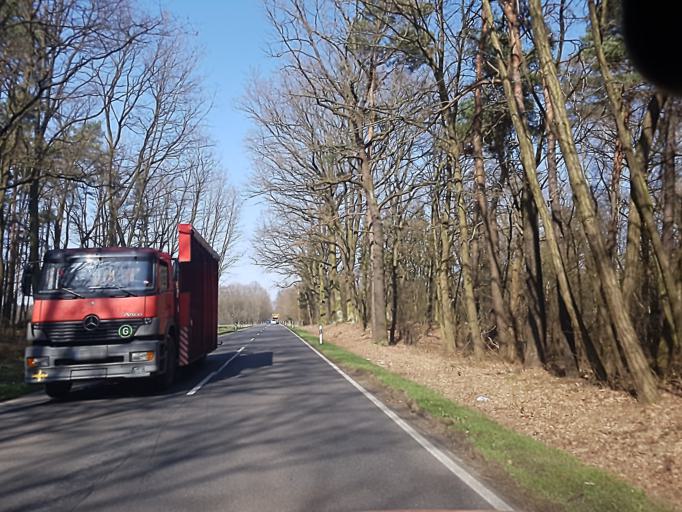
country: DE
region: Brandenburg
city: Tschernitz
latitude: 51.6607
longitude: 14.5909
